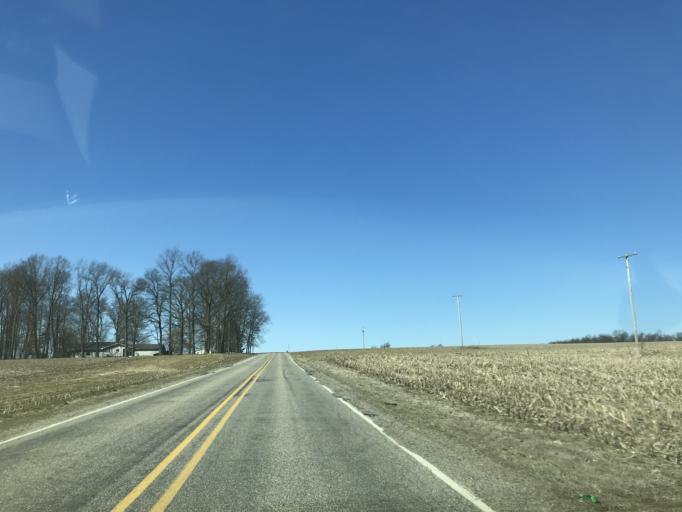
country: US
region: Michigan
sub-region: Hillsdale County
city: Jonesville
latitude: 41.9855
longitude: -84.6939
